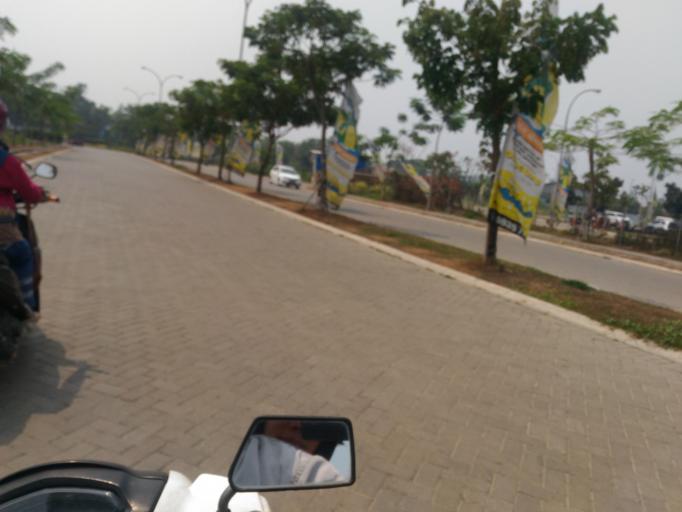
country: ID
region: West Java
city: Pasarkemis
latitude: -6.1397
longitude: 106.5413
